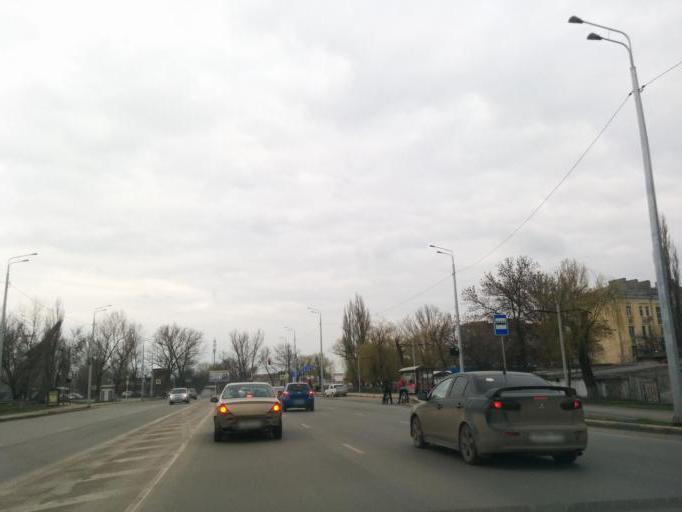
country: RU
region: Rostov
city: Novocherkassk
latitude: 47.4478
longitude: 40.1025
